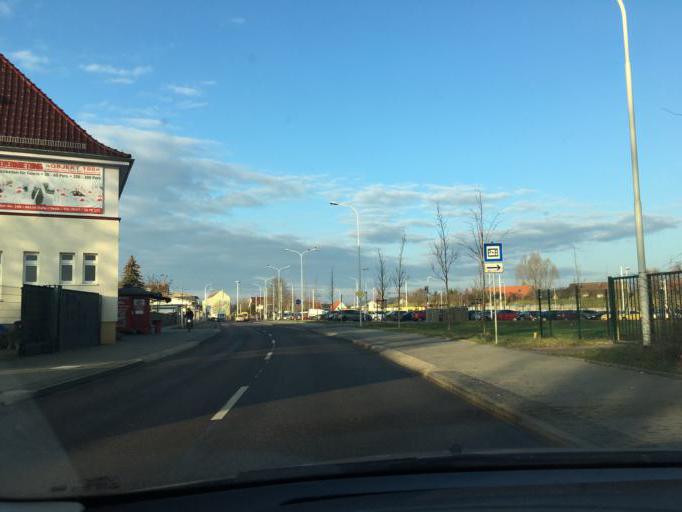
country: DE
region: Saxony-Anhalt
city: Dolbau
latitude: 51.4787
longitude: 12.0368
